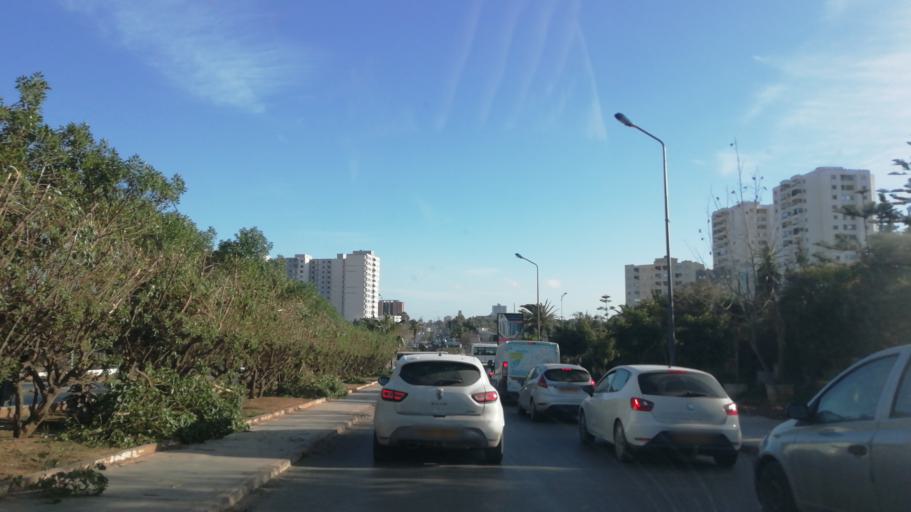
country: DZ
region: Oran
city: Bir el Djir
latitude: 35.7156
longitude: -0.5784
